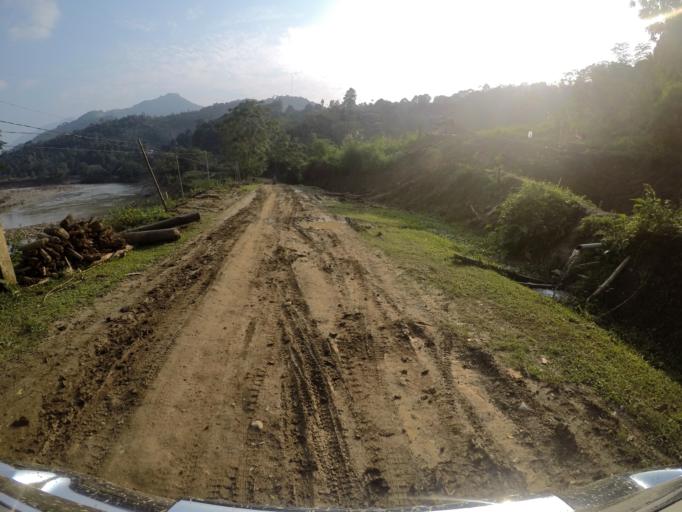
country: VN
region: Yen Bai
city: Son Thinh
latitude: 21.6858
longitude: 104.6267
